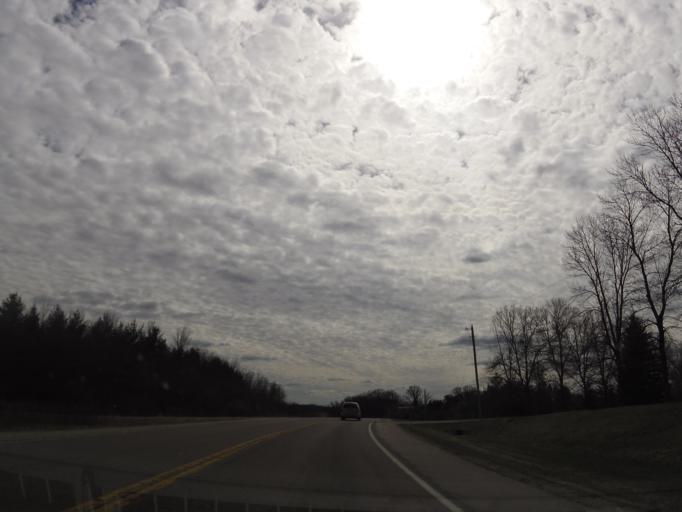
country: US
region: Minnesota
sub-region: Olmsted County
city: Stewartville
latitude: 43.8992
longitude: -92.4090
